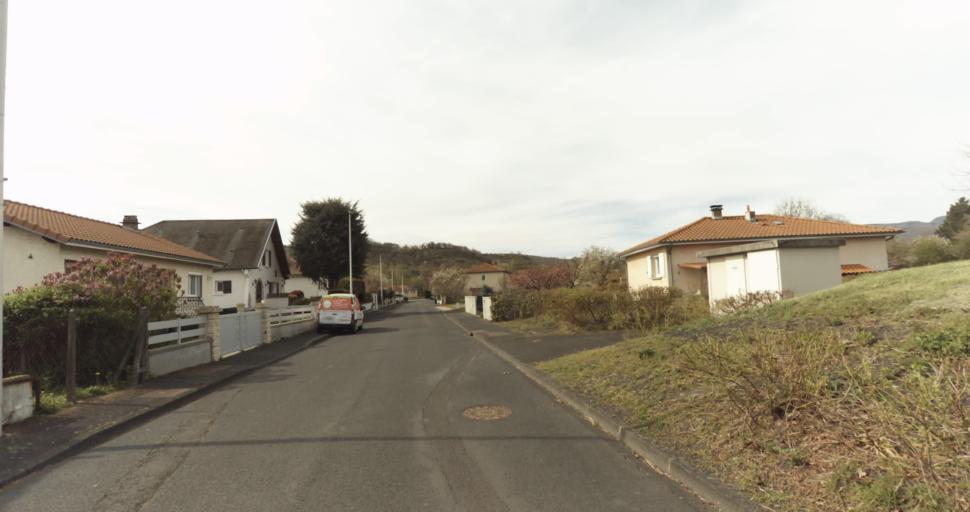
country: FR
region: Auvergne
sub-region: Departement du Puy-de-Dome
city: Cebazat
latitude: 45.8334
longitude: 3.0949
